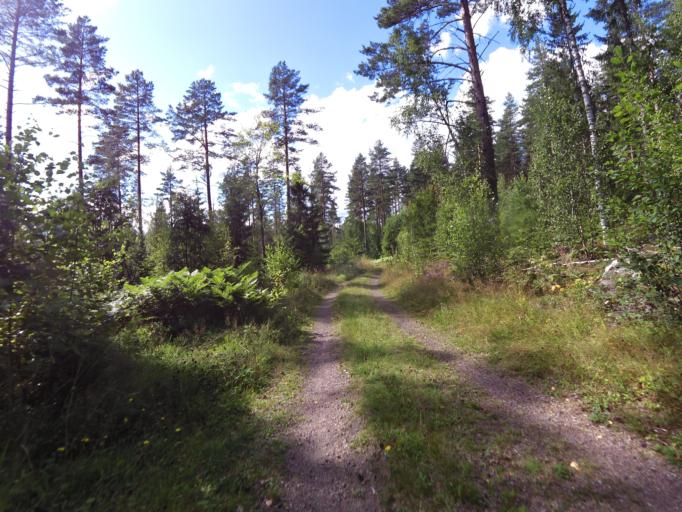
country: SE
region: Gaevleborg
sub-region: Hofors Kommun
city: Hofors
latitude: 60.5440
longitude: 16.2531
